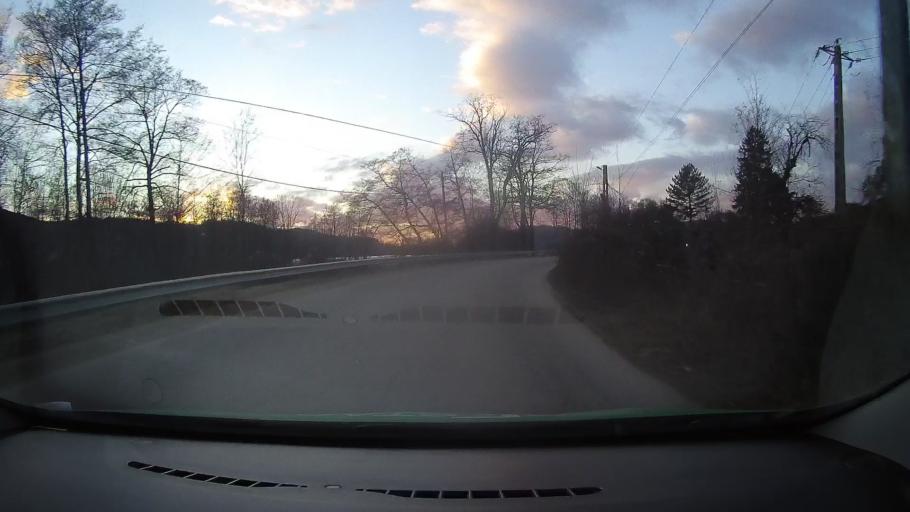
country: RO
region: Dambovita
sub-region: Comuna Valea Lunga
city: Valea Lunga Ogrea
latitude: 45.0587
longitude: 25.5966
